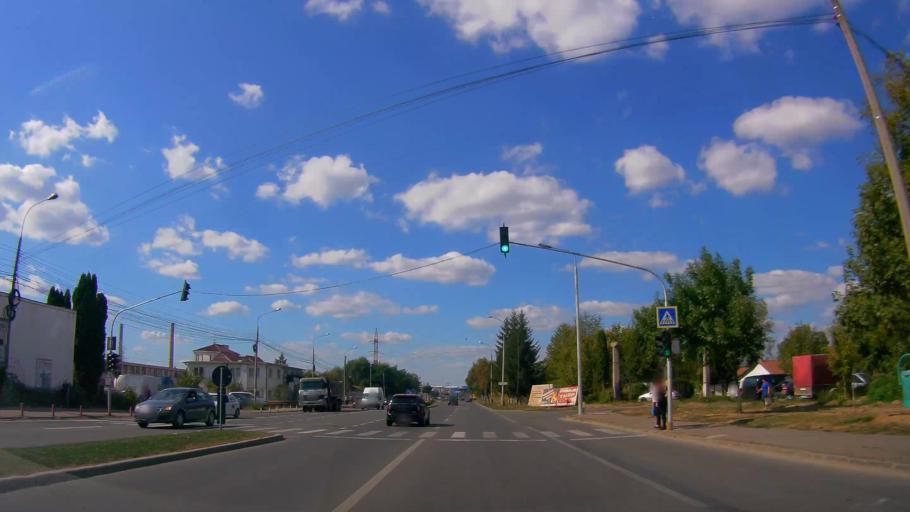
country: RO
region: Salaj
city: Zalau
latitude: 47.2043
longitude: 23.0500
